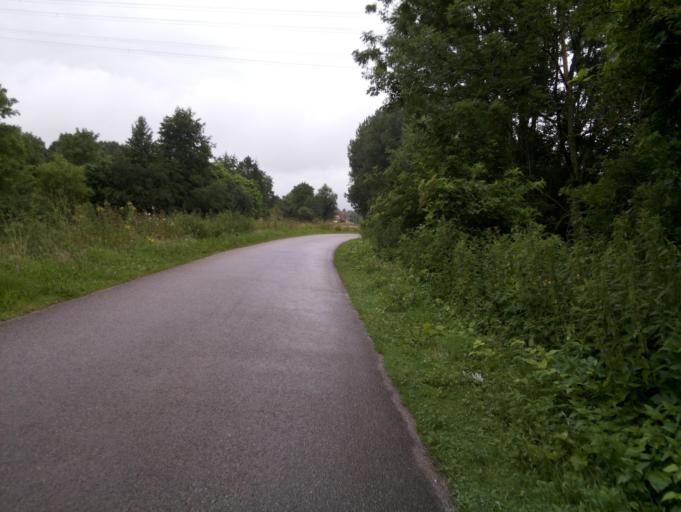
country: FR
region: Picardie
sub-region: Departement de la Somme
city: Saint-Sauveur
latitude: 49.9235
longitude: 2.2116
